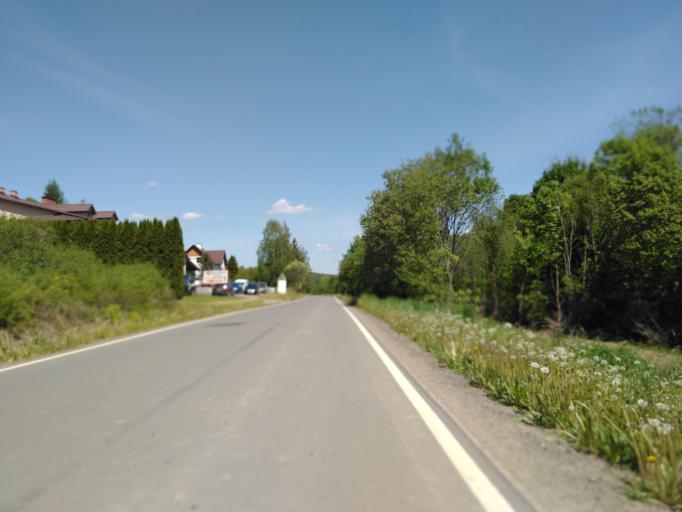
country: PL
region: Subcarpathian Voivodeship
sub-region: Powiat krosnienski
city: Dukla
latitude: 49.5867
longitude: 21.6969
